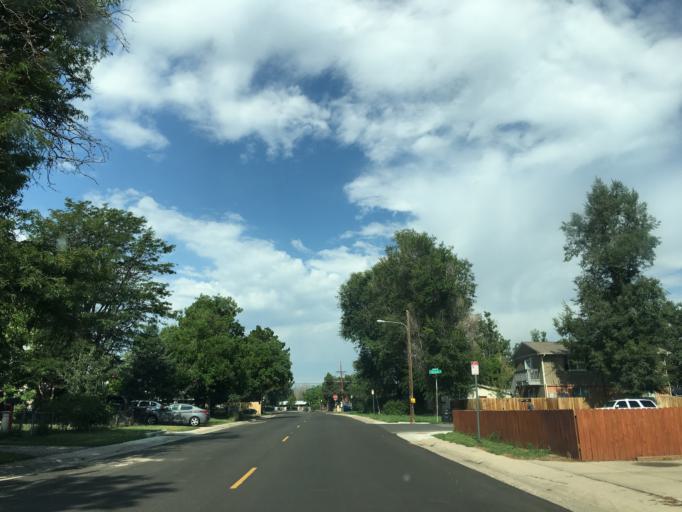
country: US
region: Colorado
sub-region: Jefferson County
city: Lakewood
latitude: 39.7040
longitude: -105.0376
